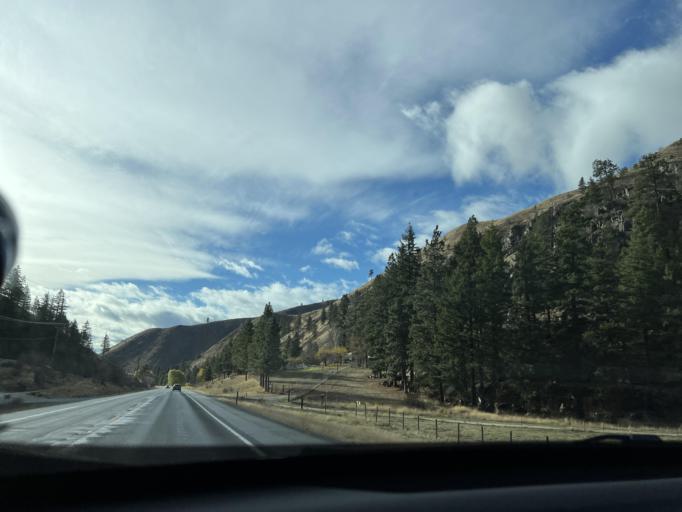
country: US
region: Washington
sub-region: Chelan County
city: Manson
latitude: 47.8153
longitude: -120.1312
